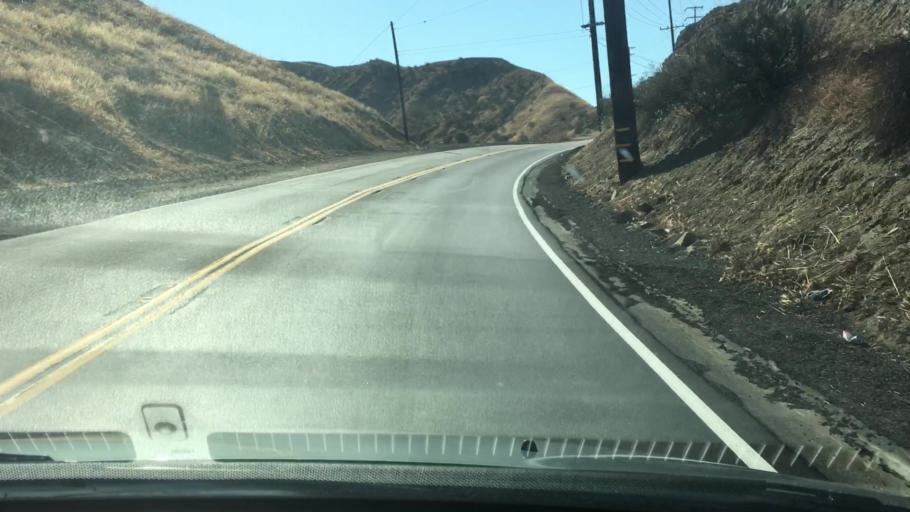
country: US
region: California
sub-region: Los Angeles County
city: Agua Dulce
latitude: 34.4739
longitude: -118.4433
